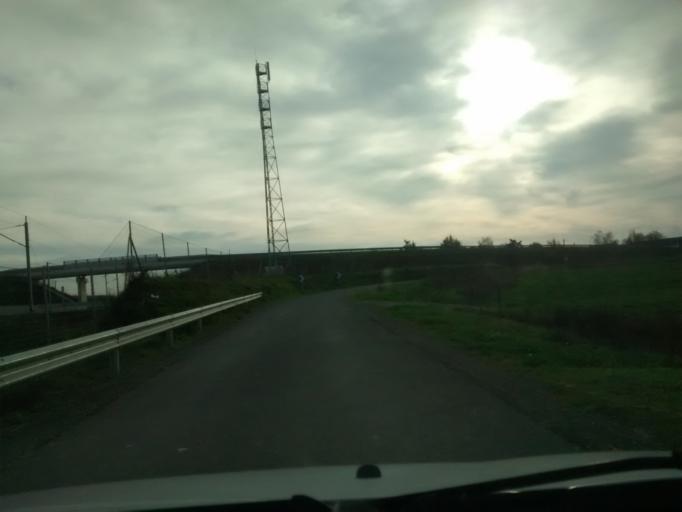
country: FR
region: Brittany
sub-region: Departement d'Ille-et-Vilaine
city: Noyal-sur-Vilaine
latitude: 48.0893
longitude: -1.5313
